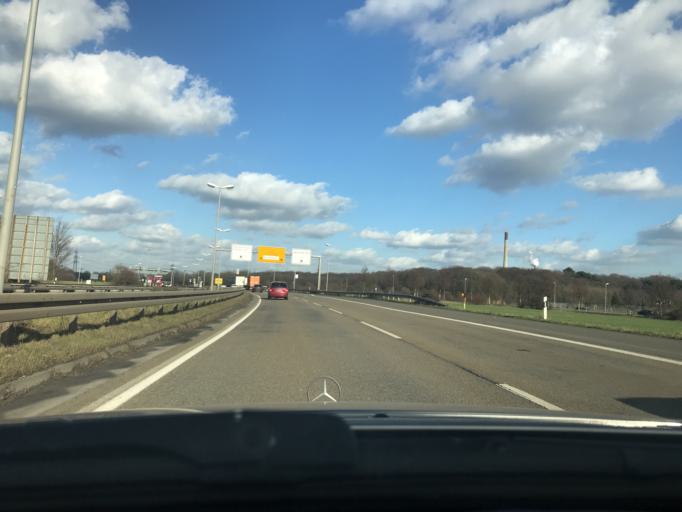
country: DE
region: North Rhine-Westphalia
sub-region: Regierungsbezirk Dusseldorf
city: Krefeld
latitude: 51.3735
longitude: 6.6381
